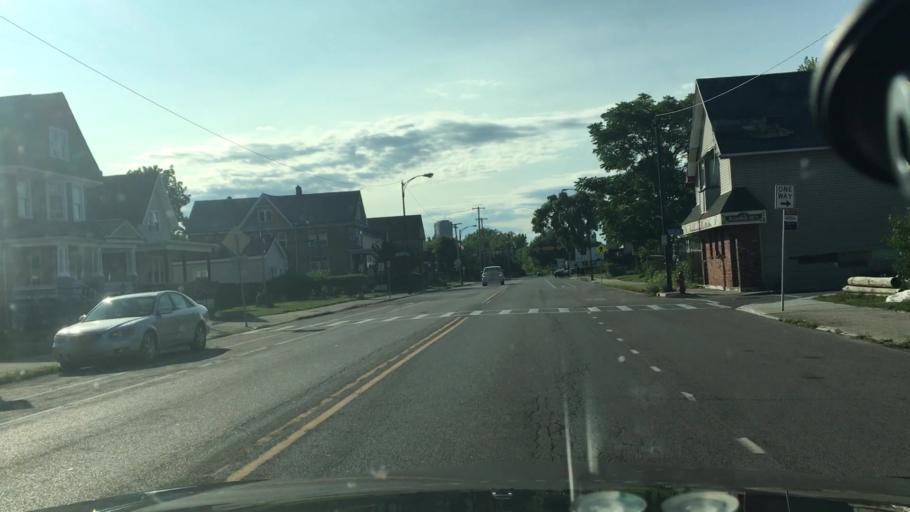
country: US
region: New York
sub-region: Erie County
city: Buffalo
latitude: 42.8668
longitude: -78.8489
